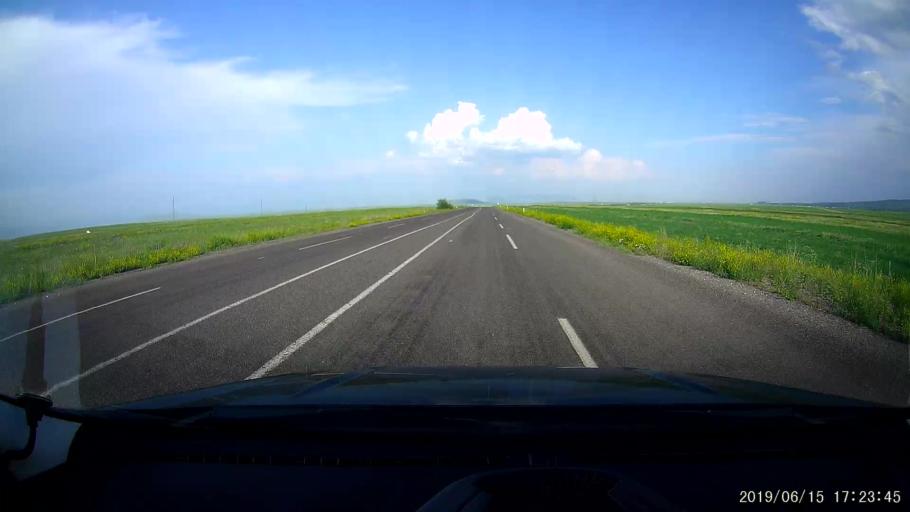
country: TR
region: Kars
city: Basgedikler
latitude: 40.6165
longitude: 43.3698
